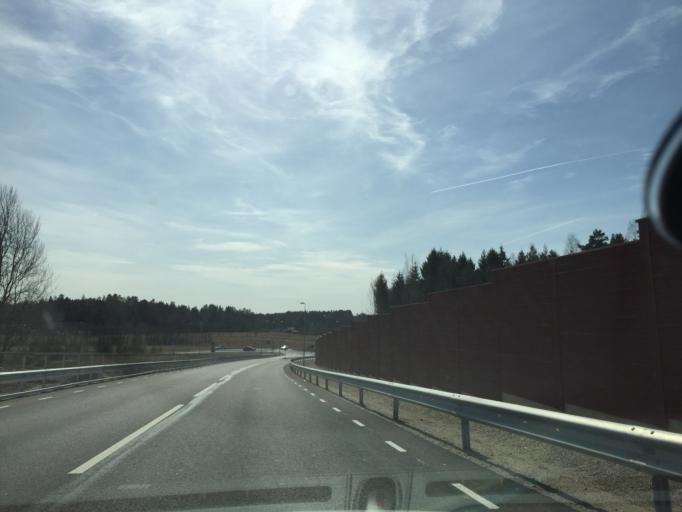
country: SE
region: Vaestra Goetaland
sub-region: Uddevalla Kommun
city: Uddevalla
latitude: 58.3522
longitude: 11.8020
